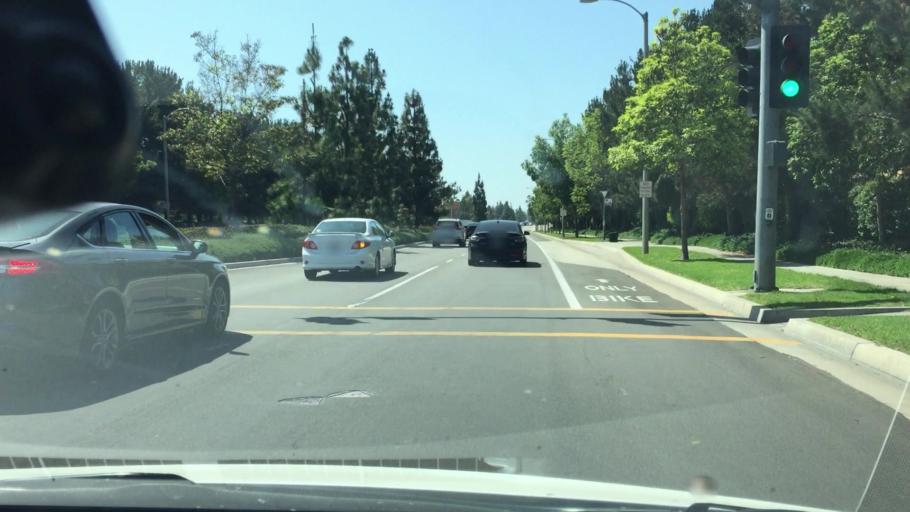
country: US
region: California
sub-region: Orange County
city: North Tustin
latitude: 33.7202
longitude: -117.7825
